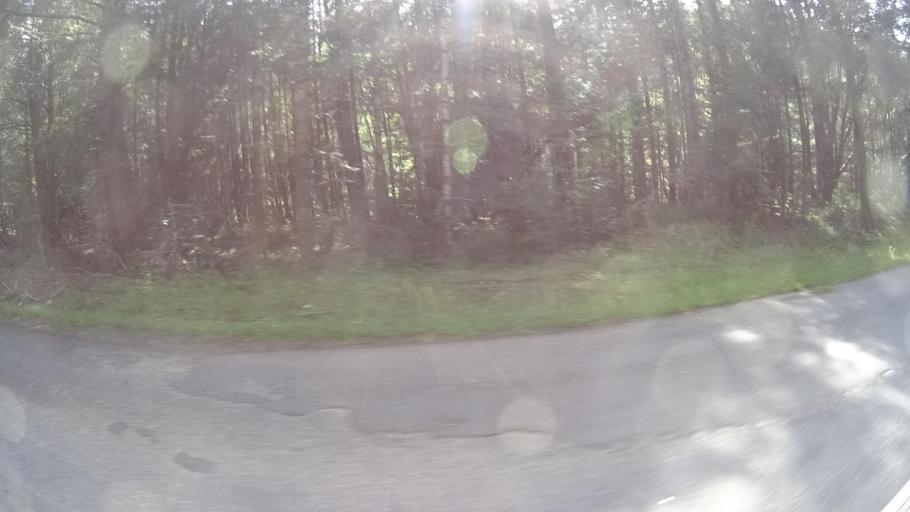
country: US
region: California
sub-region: Humboldt County
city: Rio Dell
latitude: 40.4441
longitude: -123.7935
